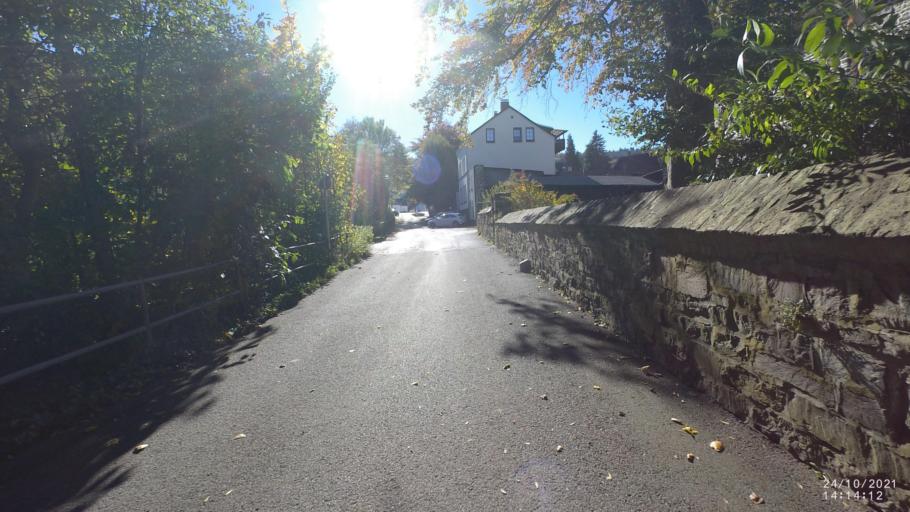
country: DE
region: North Rhine-Westphalia
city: Hemer
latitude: 51.3754
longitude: 7.7563
